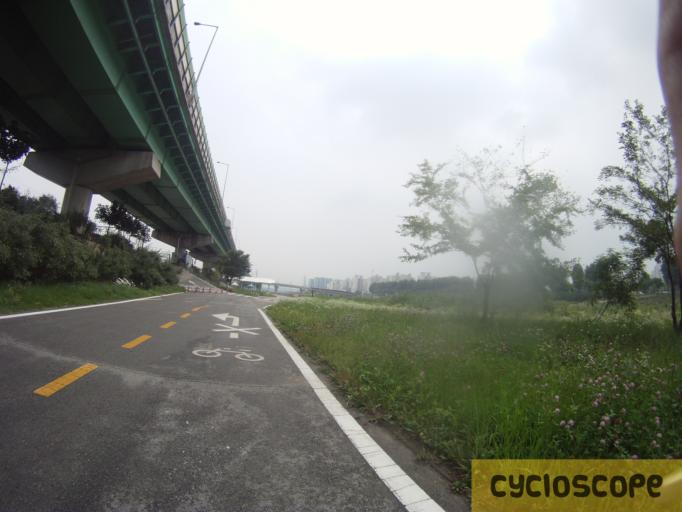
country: KR
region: Gyeonggi-do
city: Kwangmyong
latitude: 37.4560
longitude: 126.8930
